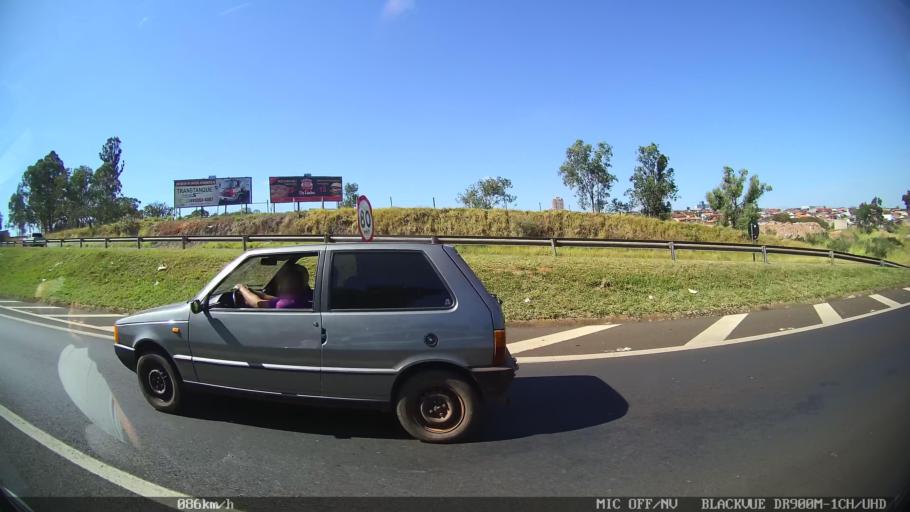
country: BR
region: Sao Paulo
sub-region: Franca
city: Franca
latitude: -20.5325
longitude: -47.4243
